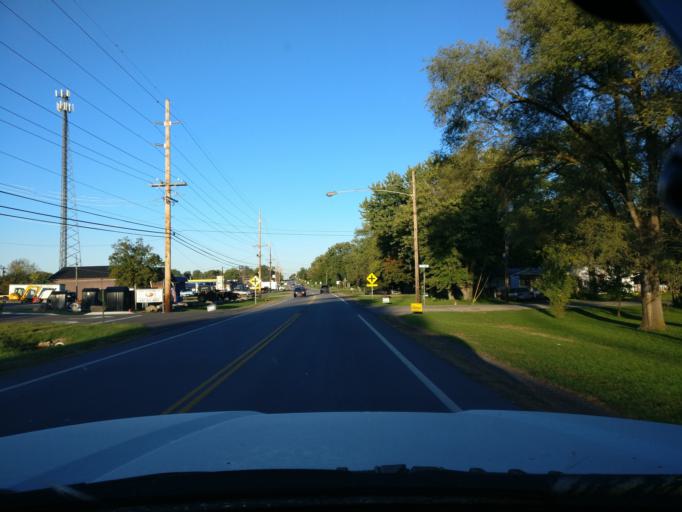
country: US
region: Ohio
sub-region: Warren County
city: Hunter
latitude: 39.4925
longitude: -84.2772
